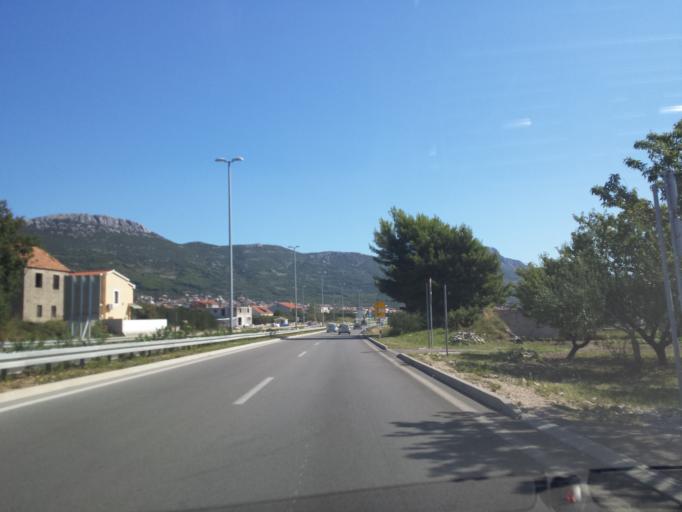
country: HR
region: Splitsko-Dalmatinska
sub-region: Grad Trogir
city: Trogir
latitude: 43.5548
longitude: 16.3231
